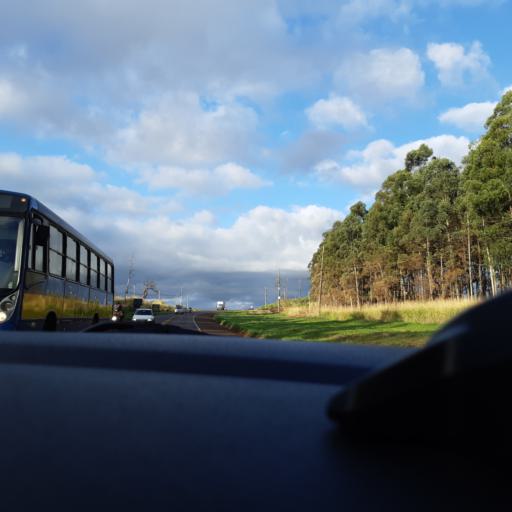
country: BR
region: Sao Paulo
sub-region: Ourinhos
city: Ourinhos
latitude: -22.9948
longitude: -49.8493
